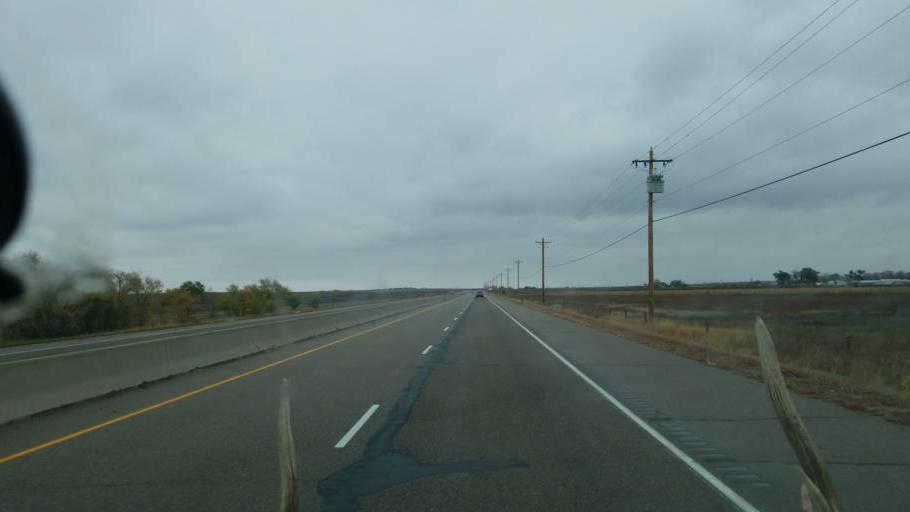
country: US
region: Colorado
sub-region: Pueblo County
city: Pueblo
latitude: 38.2732
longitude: -104.4433
